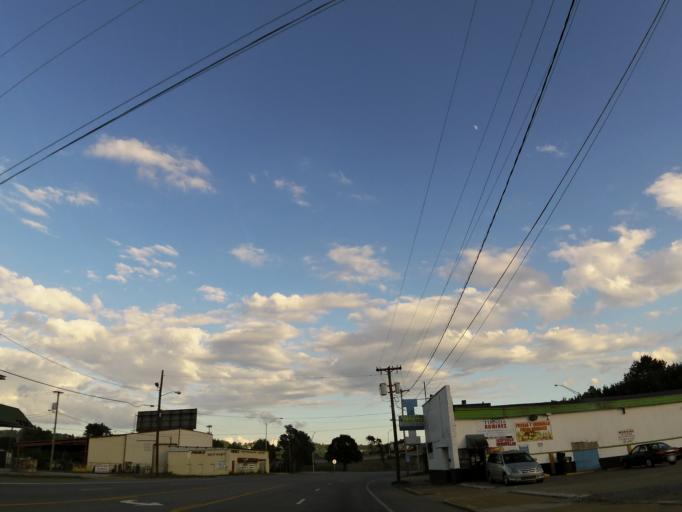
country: US
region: Tennessee
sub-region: Hamilton County
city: Chattanooga
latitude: 35.0208
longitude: -85.2946
